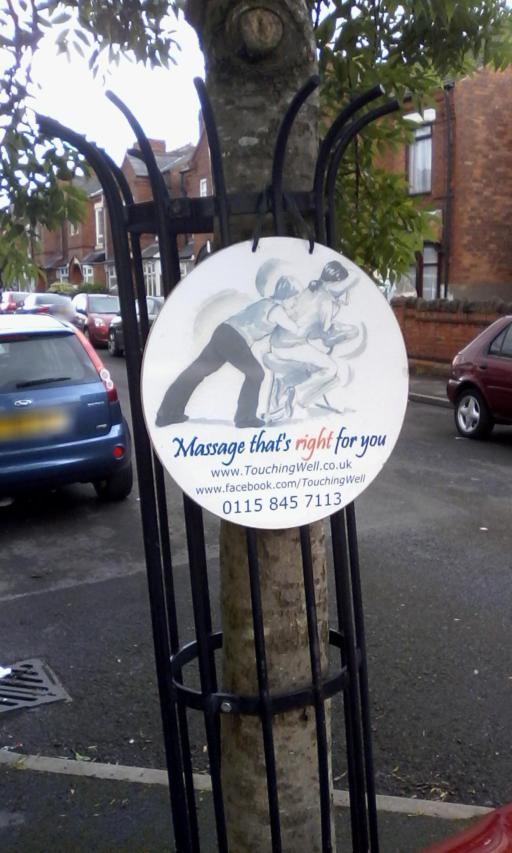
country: GB
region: England
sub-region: Nottinghamshire
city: West Bridgford
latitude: 52.9665
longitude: -1.1102
